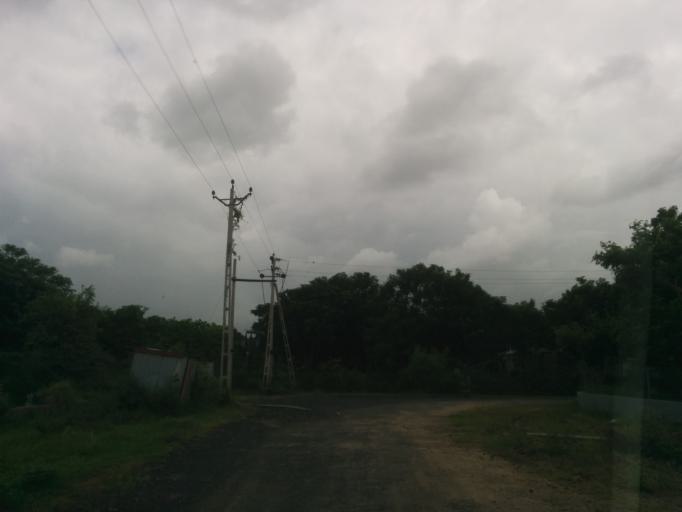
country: IN
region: Gujarat
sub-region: Ahmadabad
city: Sanand
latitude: 23.0762
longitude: 72.3866
